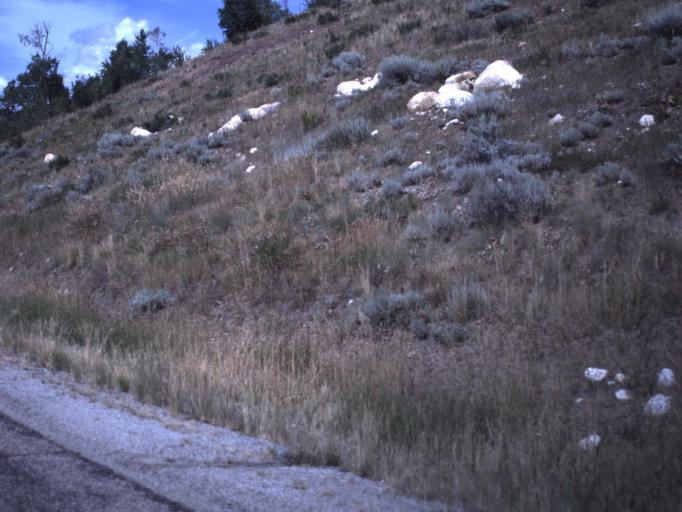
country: US
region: Utah
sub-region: Cache County
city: Richmond
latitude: 41.9095
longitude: -111.5626
